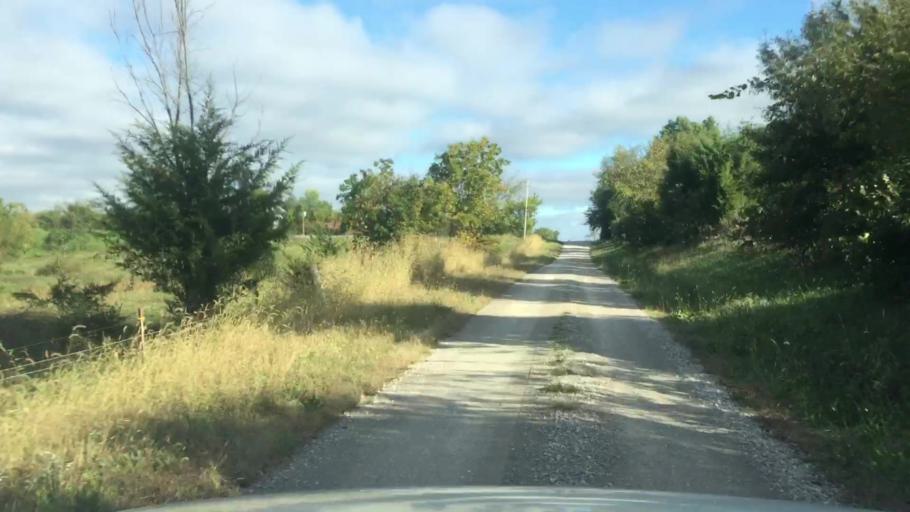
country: US
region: Missouri
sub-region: Howard County
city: New Franklin
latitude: 39.0924
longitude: -92.7797
